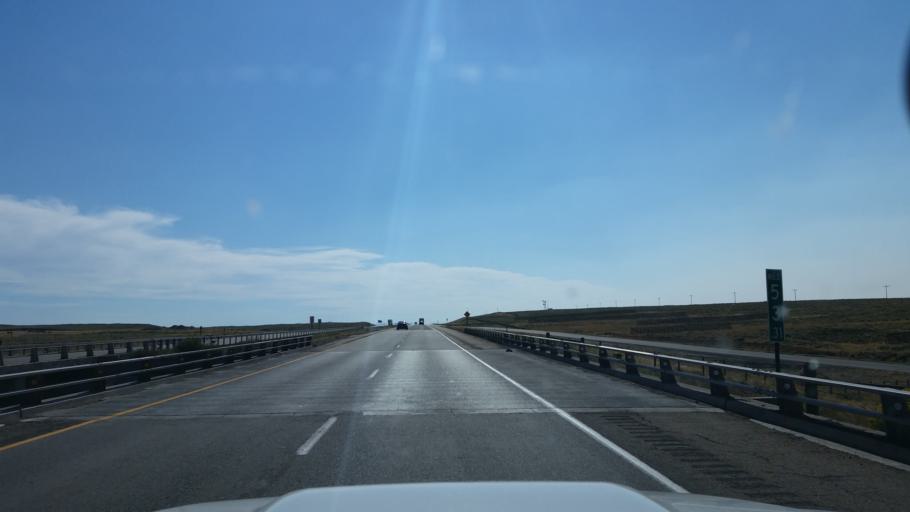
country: US
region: Wyoming
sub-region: Uinta County
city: Lyman
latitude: 41.4334
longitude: -110.1082
